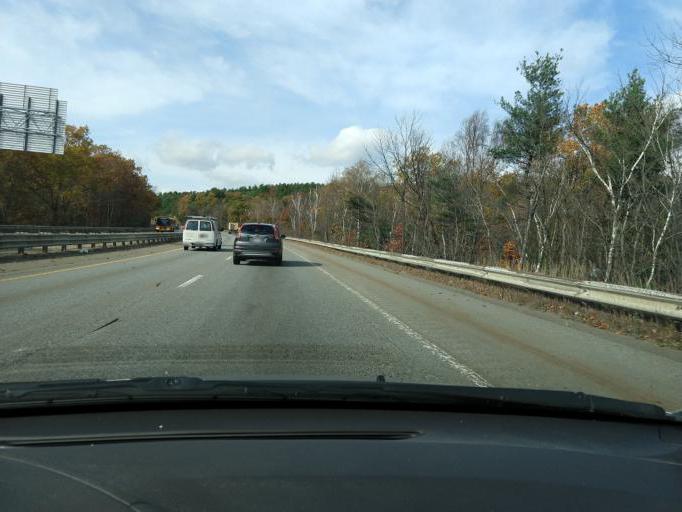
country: US
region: Massachusetts
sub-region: Middlesex County
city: Littleton Common
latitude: 42.5281
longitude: -71.5247
